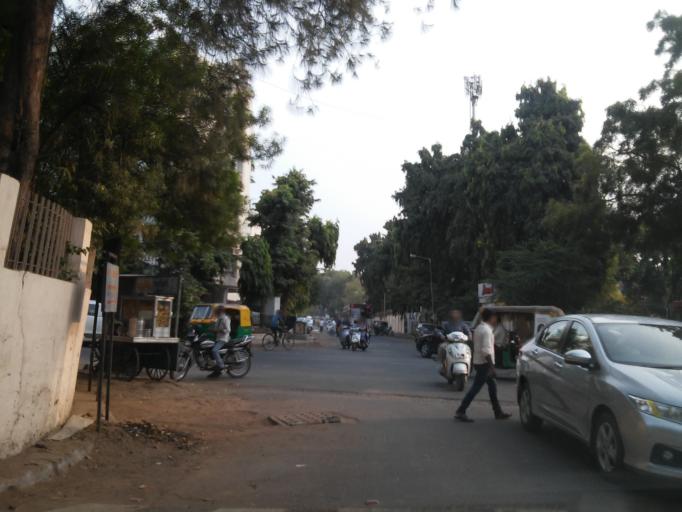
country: IN
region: Gujarat
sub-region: Ahmadabad
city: Ahmedabad
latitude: 23.0106
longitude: 72.5574
